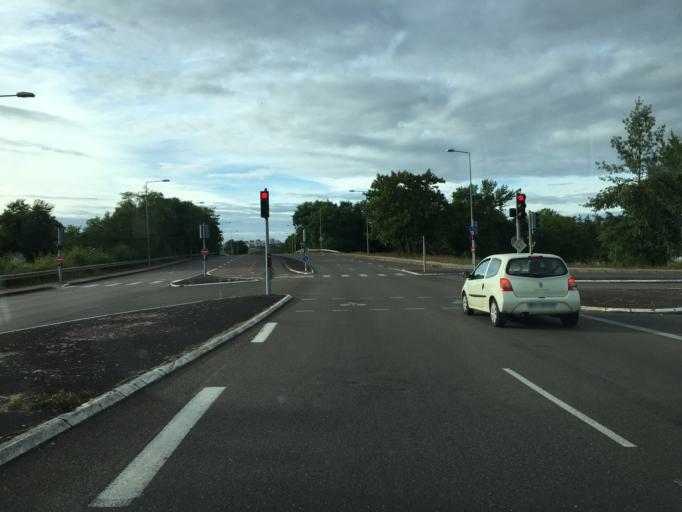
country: FR
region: Bourgogne
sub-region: Departement de la Cote-d'Or
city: Dijon
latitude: 47.3159
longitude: 5.0132
